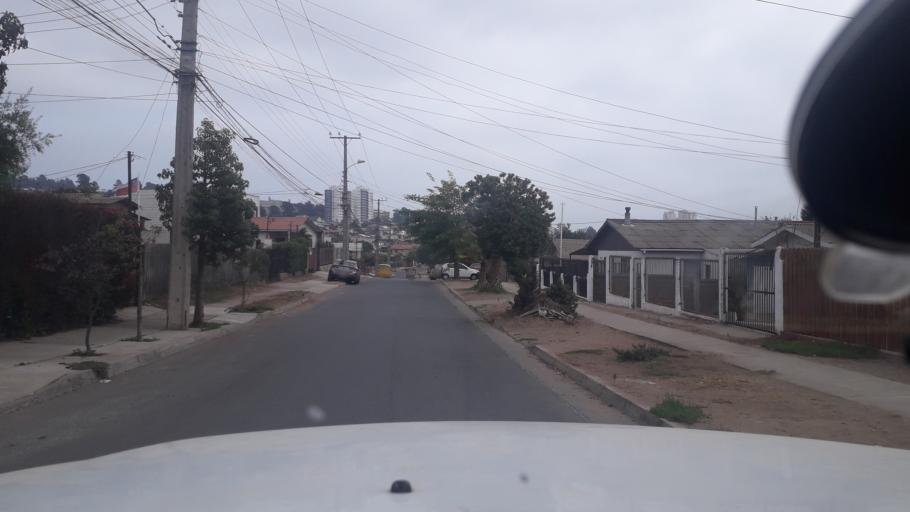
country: CL
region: Valparaiso
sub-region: Provincia de Valparaiso
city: Vina del Mar
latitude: -32.9347
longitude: -71.5231
